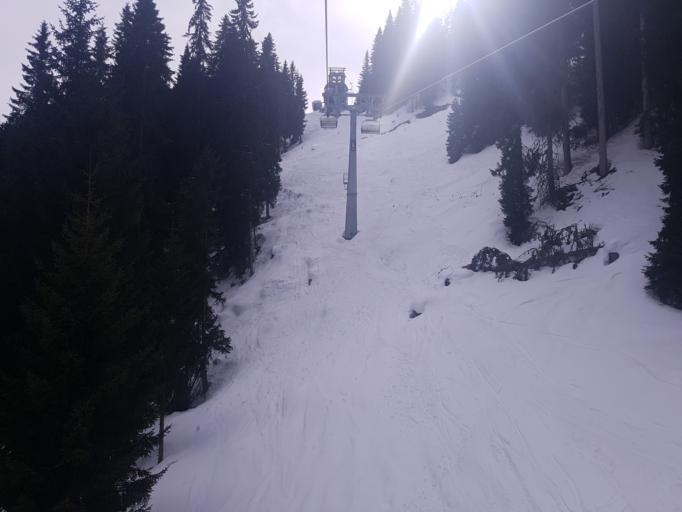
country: AT
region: Tyrol
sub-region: Politischer Bezirk Kufstein
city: Worgl
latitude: 47.4336
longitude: 12.0829
